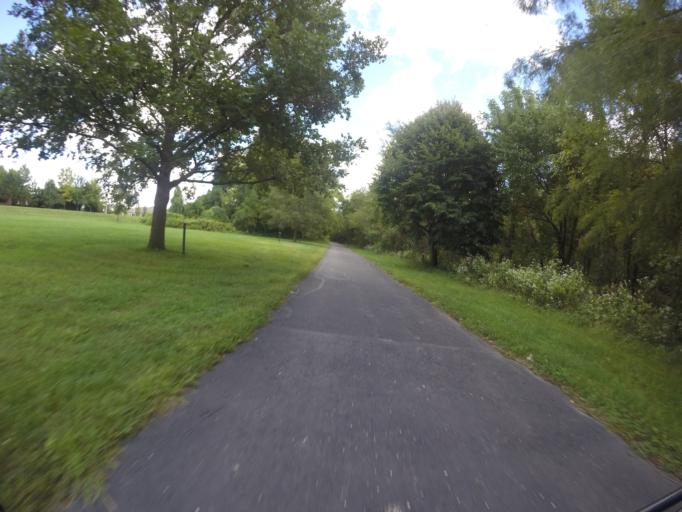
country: US
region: Kansas
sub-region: Johnson County
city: Lenexa
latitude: 38.9124
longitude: -94.7214
